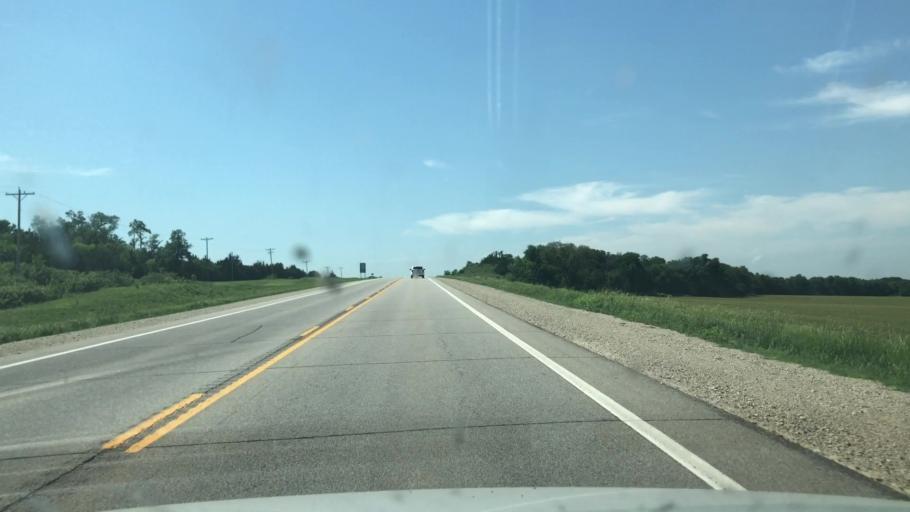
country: US
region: Kansas
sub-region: Cowley County
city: Winfield
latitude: 37.3740
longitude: -97.0071
